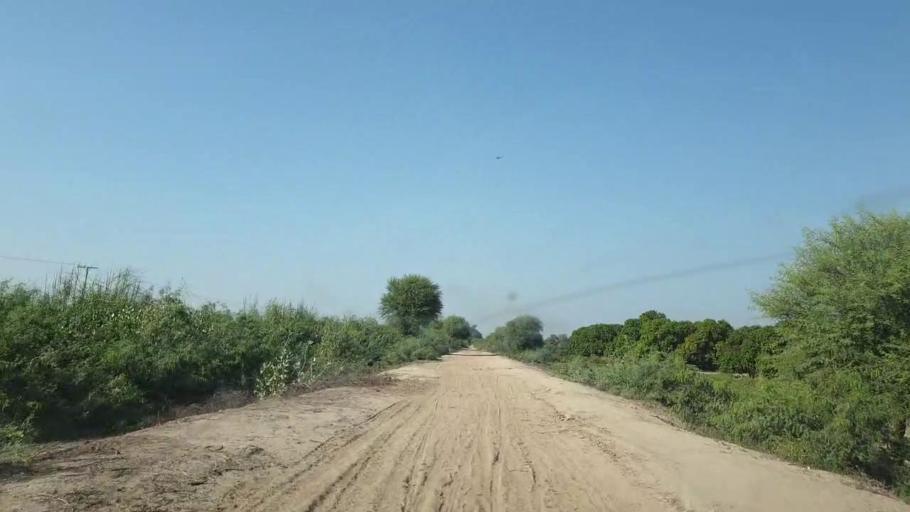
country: PK
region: Sindh
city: Tando Jam
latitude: 25.3662
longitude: 68.5693
